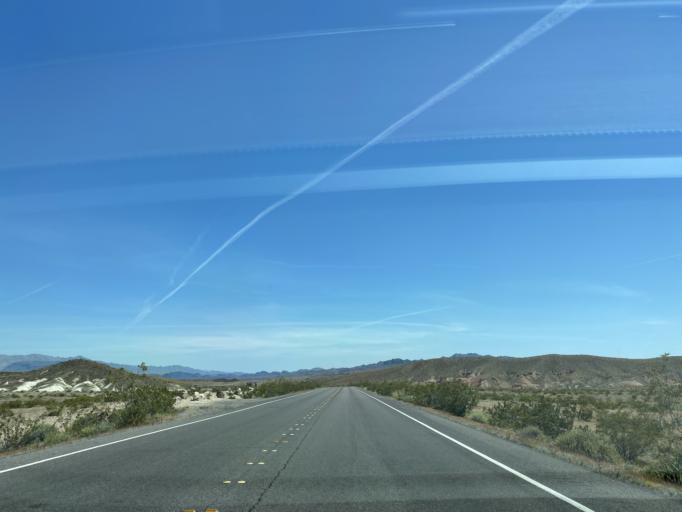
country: US
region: Nevada
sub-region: Clark County
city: Henderson
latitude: 36.1663
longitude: -114.9104
